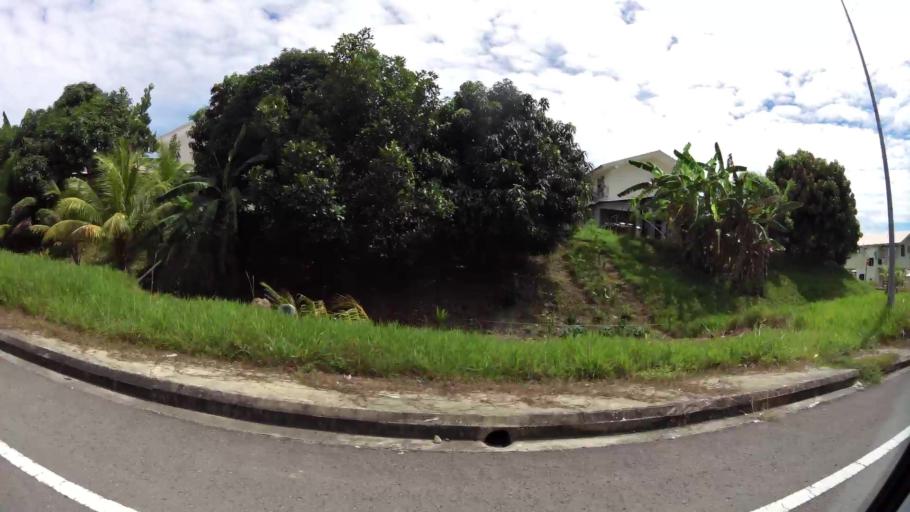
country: BN
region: Brunei and Muara
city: Bandar Seri Begawan
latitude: 4.9919
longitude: 115.0090
